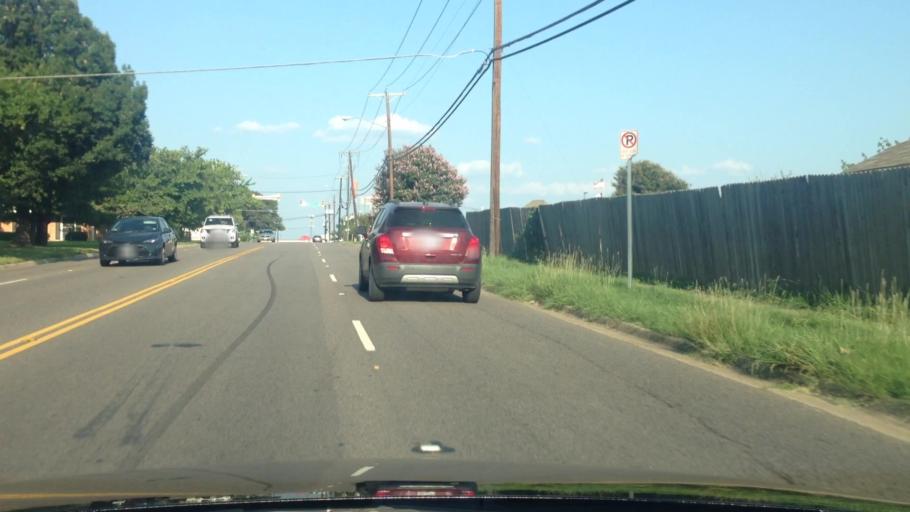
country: US
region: Texas
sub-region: Tarrant County
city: Edgecliff Village
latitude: 32.6351
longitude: -97.3263
